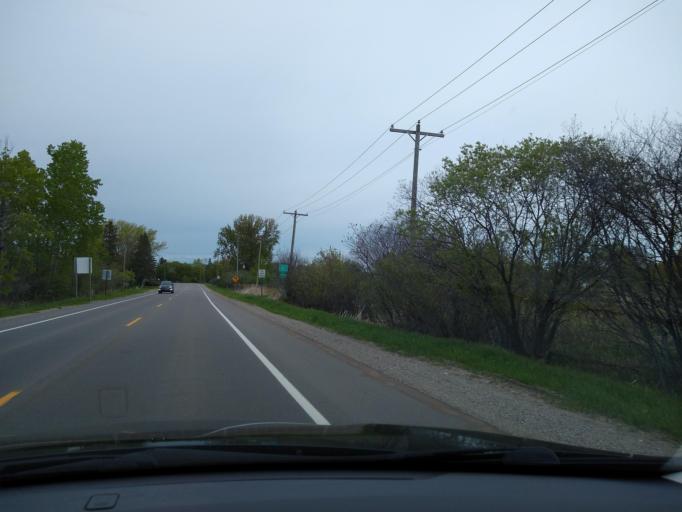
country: US
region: Michigan
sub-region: Delta County
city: Escanaba
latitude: 45.7744
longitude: -87.0701
